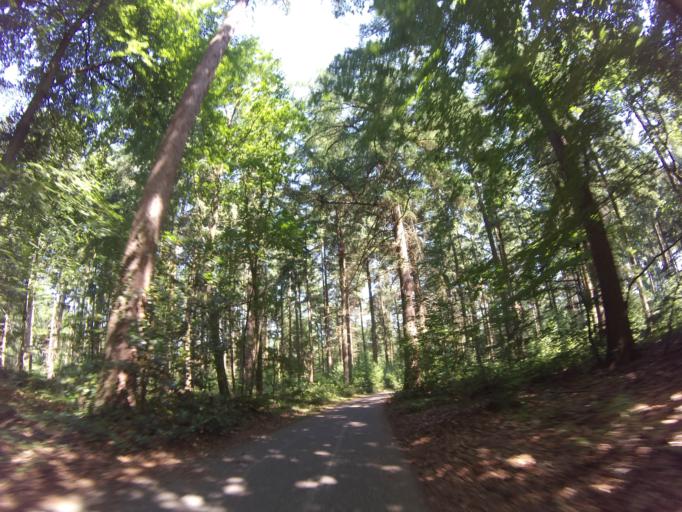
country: NL
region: Drenthe
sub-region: Gemeente Coevorden
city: Sleen
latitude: 52.8390
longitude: 6.7417
